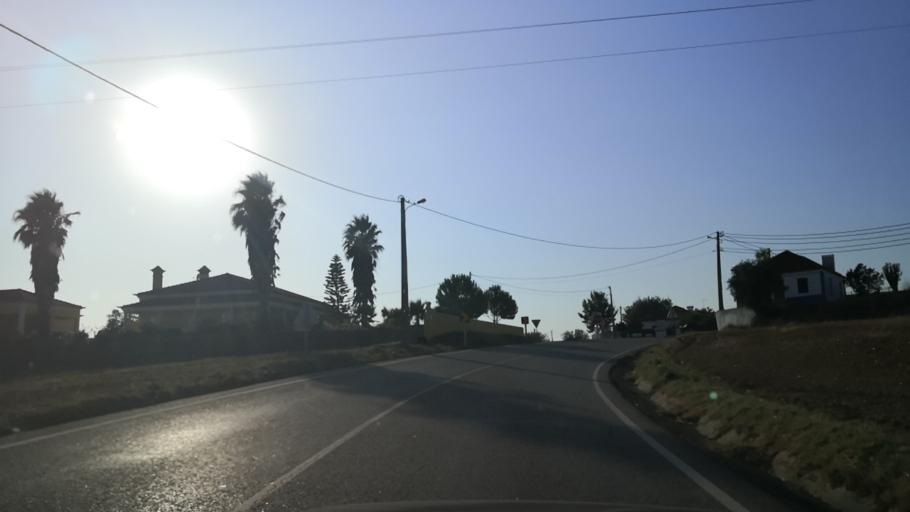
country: PT
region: Santarem
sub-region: Alcanena
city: Alcanena
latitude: 39.3470
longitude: -8.6628
